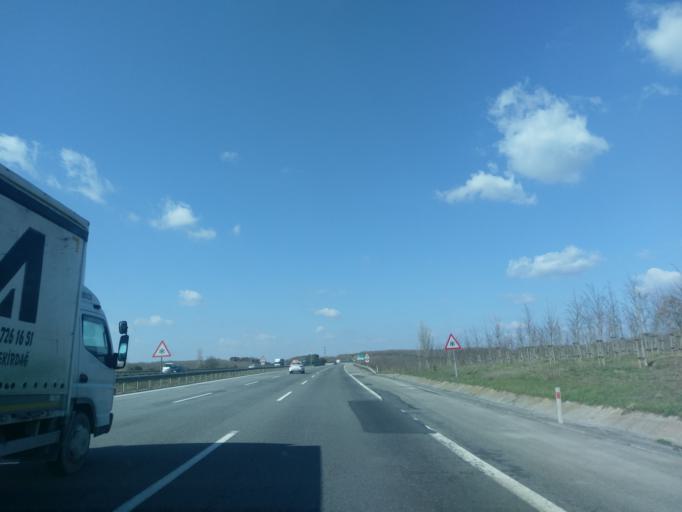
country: TR
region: Istanbul
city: Canta
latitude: 41.1768
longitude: 28.1157
